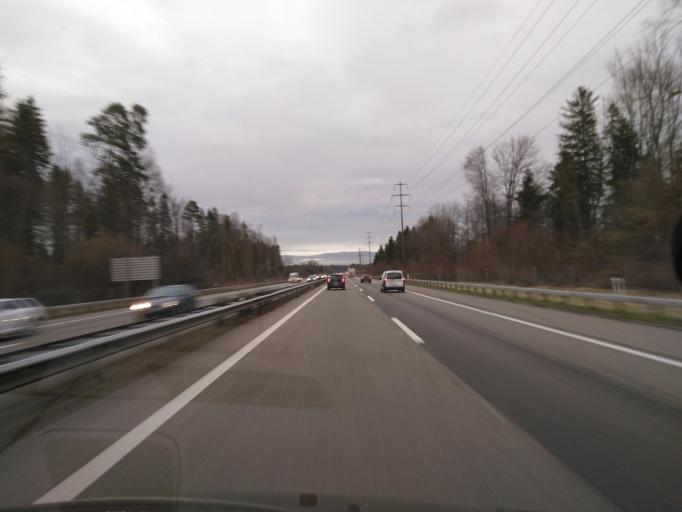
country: CH
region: Saint Gallen
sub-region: Wahlkreis Wil
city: Wil
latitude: 47.4568
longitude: 9.0744
